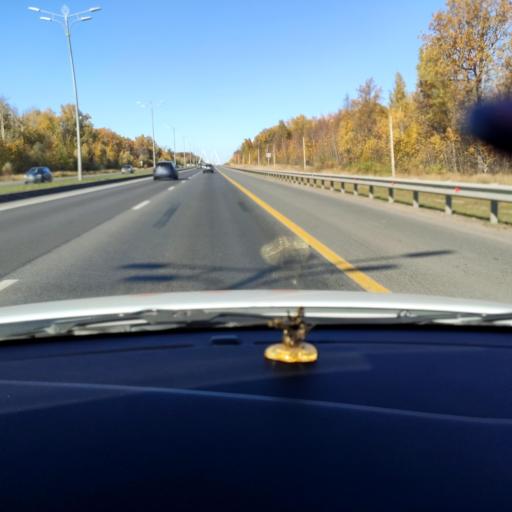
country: RU
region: Tatarstan
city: Stolbishchi
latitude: 55.7046
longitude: 49.2221
